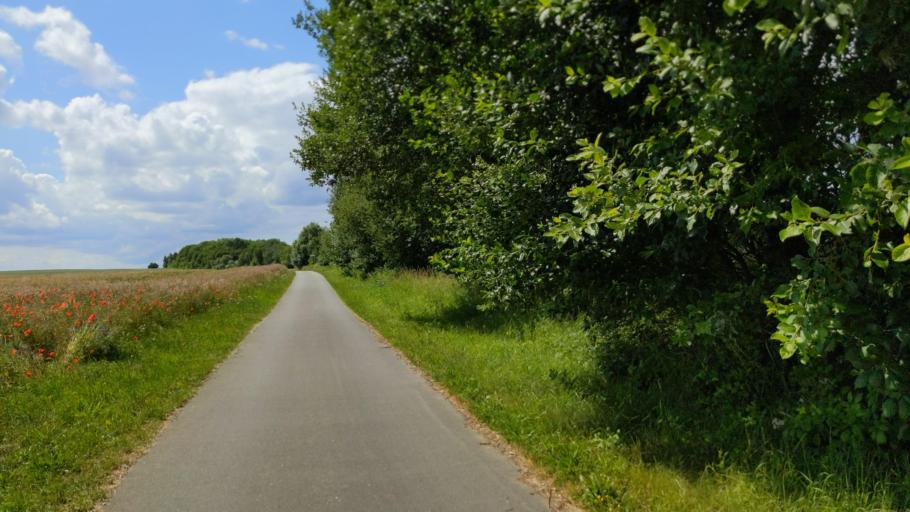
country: DE
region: Mecklenburg-Vorpommern
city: Kalkhorst
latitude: 54.0073
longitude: 11.0557
